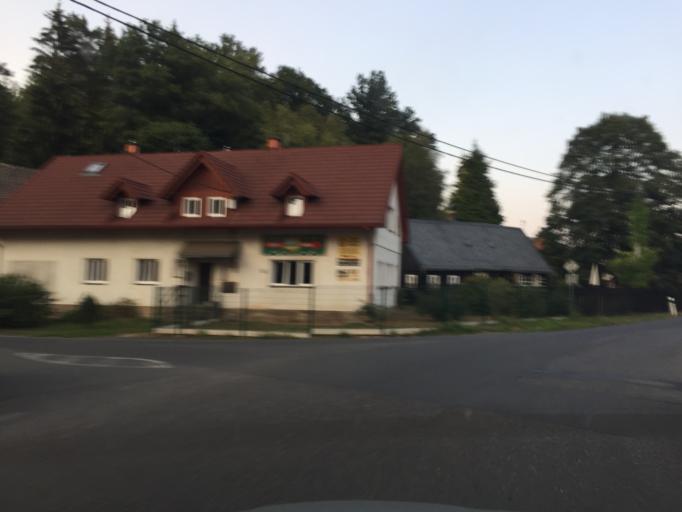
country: CZ
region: Ustecky
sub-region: Okres Decin
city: Chribska
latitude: 50.8639
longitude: 14.4530
